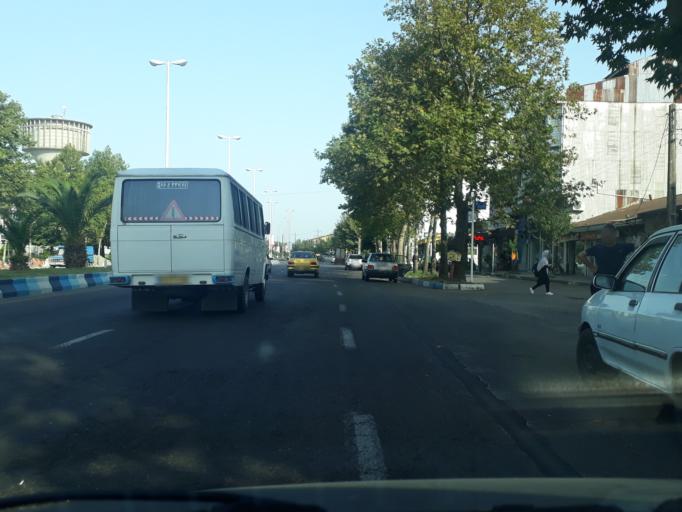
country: IR
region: Gilan
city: Bandar-e Anzali
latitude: 37.4604
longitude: 49.4945
